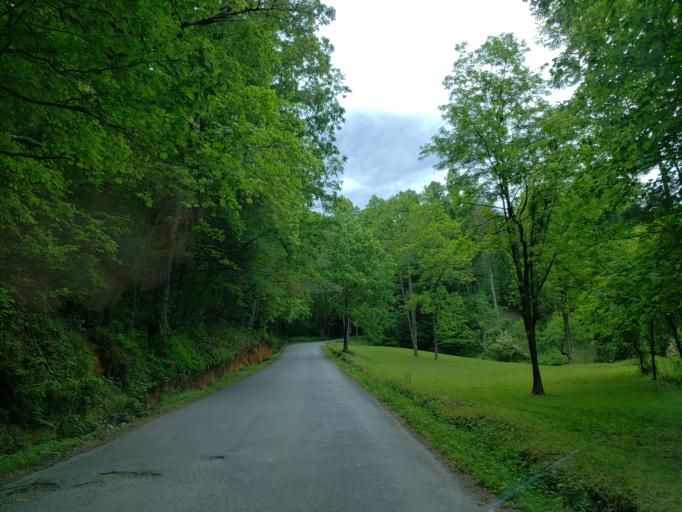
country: US
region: Georgia
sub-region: Fannin County
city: Blue Ridge
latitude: 34.8471
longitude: -84.4172
